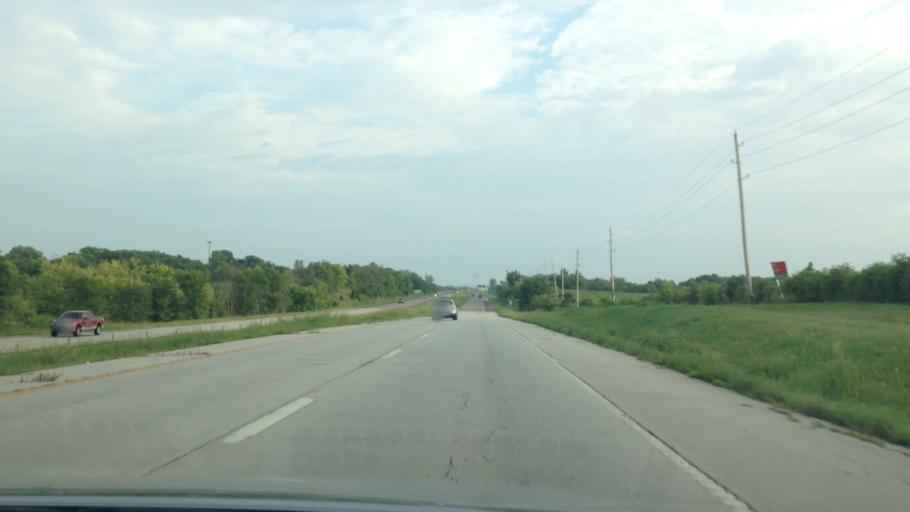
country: US
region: Missouri
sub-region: Clay County
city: Smithville
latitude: 39.3240
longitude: -94.5845
